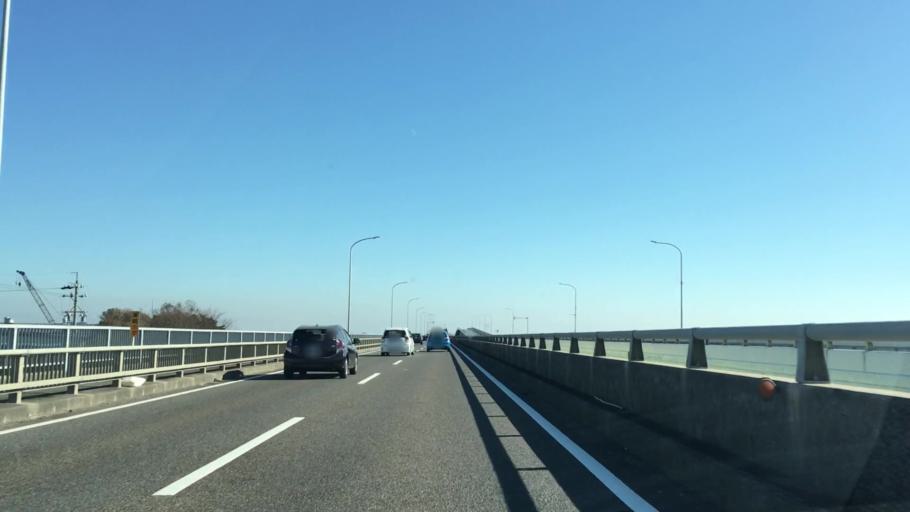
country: JP
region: Aichi
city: Tahara
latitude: 34.6938
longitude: 137.2975
